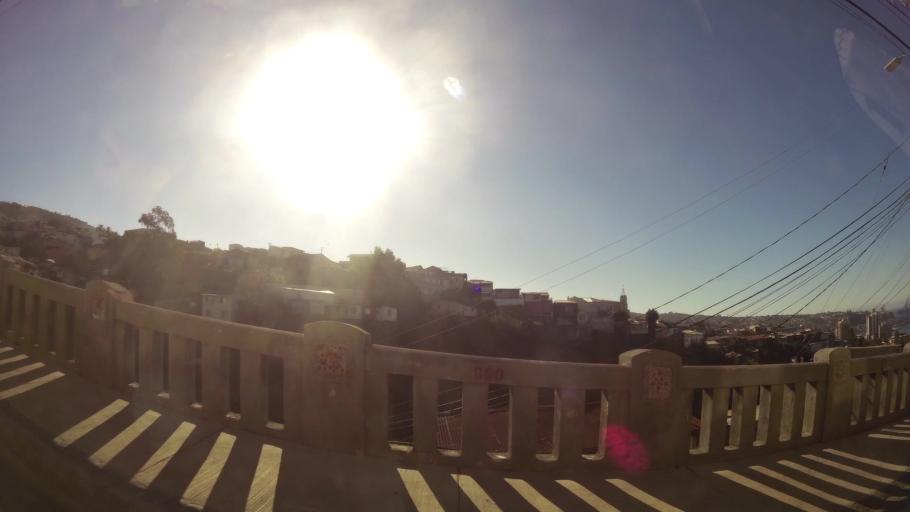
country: CL
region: Valparaiso
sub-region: Provincia de Valparaiso
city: Valparaiso
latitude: -33.0513
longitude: -71.6187
